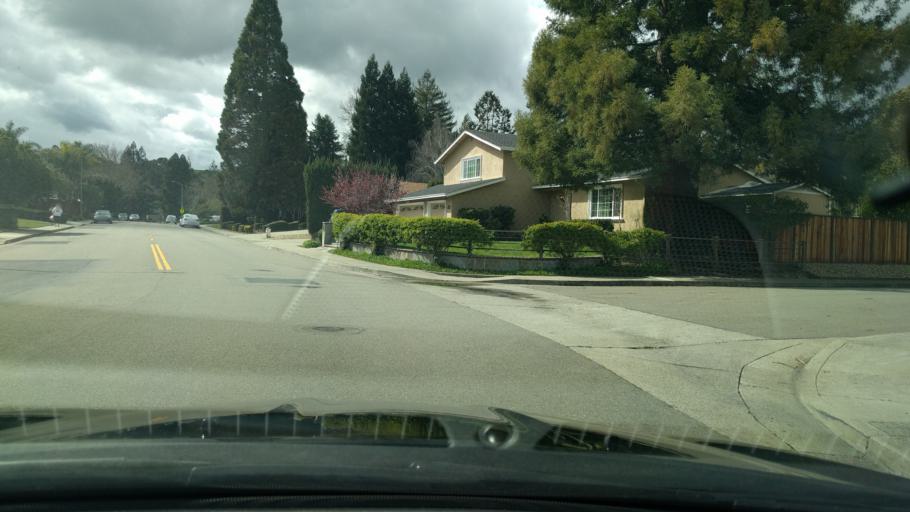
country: US
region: California
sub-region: Contra Costa County
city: San Ramon
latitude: 37.7713
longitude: -121.9851
